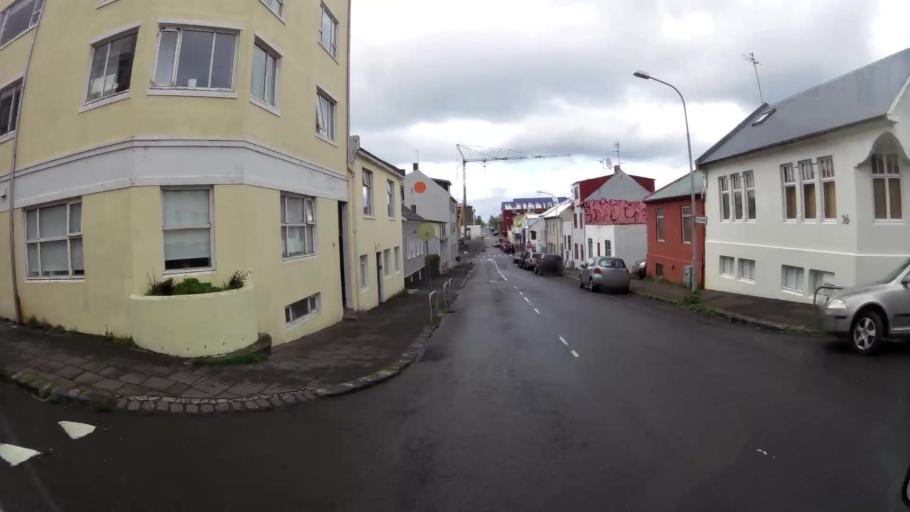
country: IS
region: Capital Region
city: Seltjarnarnes
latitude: 64.1503
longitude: -21.9563
